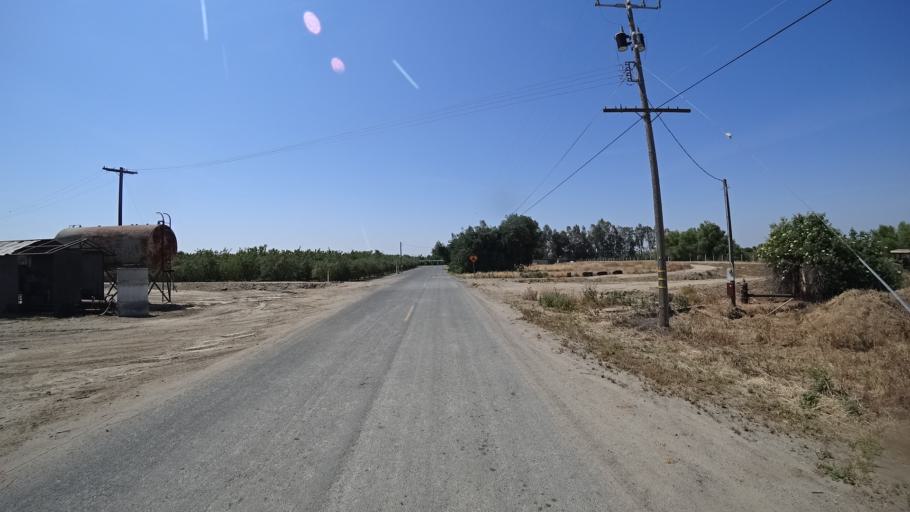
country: US
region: California
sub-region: Fresno County
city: Riverdale
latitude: 36.3896
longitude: -119.8693
